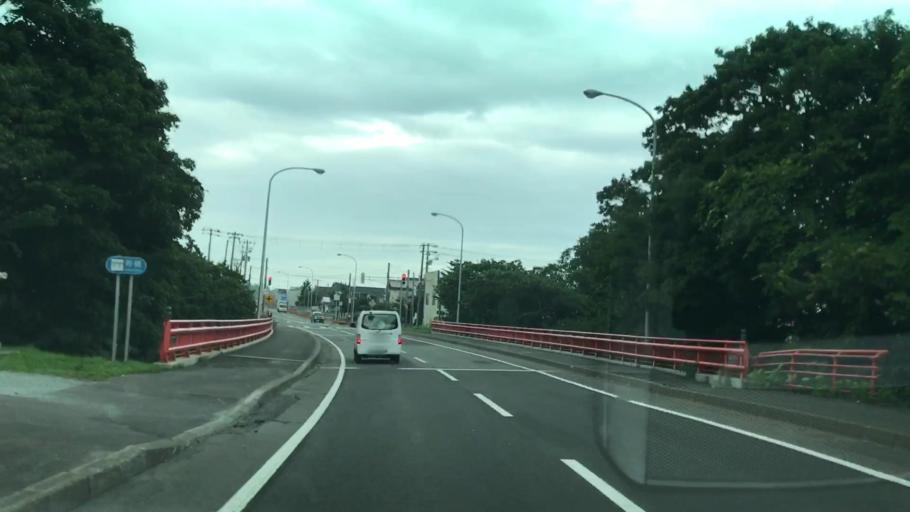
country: JP
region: Hokkaido
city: Iwanai
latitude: 42.7915
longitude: 140.2323
